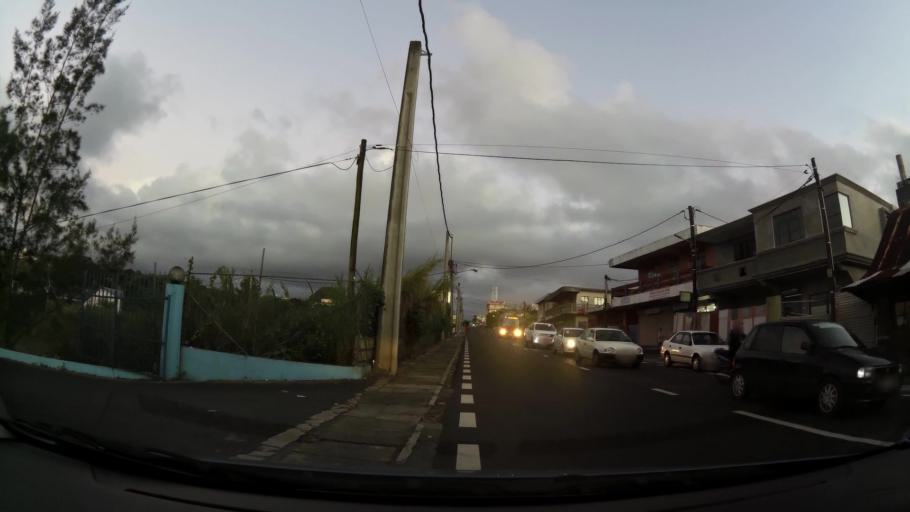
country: MU
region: Plaines Wilhems
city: Curepipe
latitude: -20.2953
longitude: 57.5189
